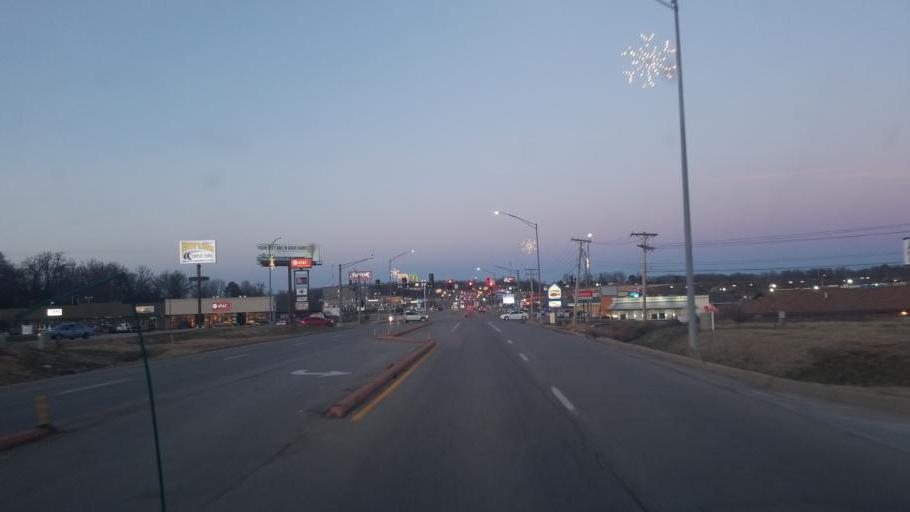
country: US
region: Missouri
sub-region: Howell County
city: West Plains
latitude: 36.7115
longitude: -91.8756
